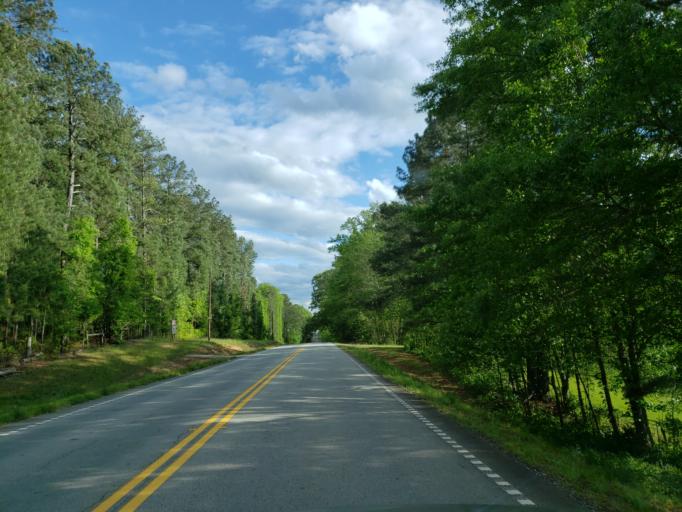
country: US
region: Georgia
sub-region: Haralson County
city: Tallapoosa
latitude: 33.7984
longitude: -85.2962
